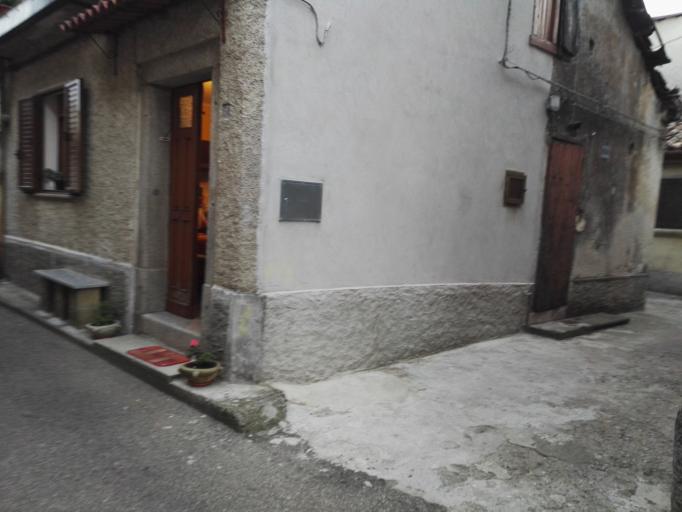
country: IT
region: Calabria
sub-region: Provincia di Vibo-Valentia
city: Serra San Bruno
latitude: 38.5739
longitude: 16.3282
